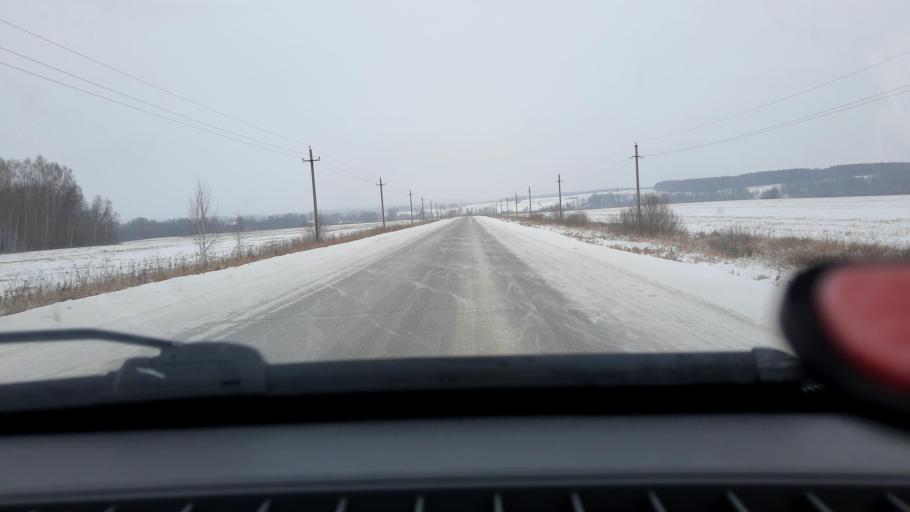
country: RU
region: Bashkortostan
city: Iglino
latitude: 54.6921
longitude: 56.4153
